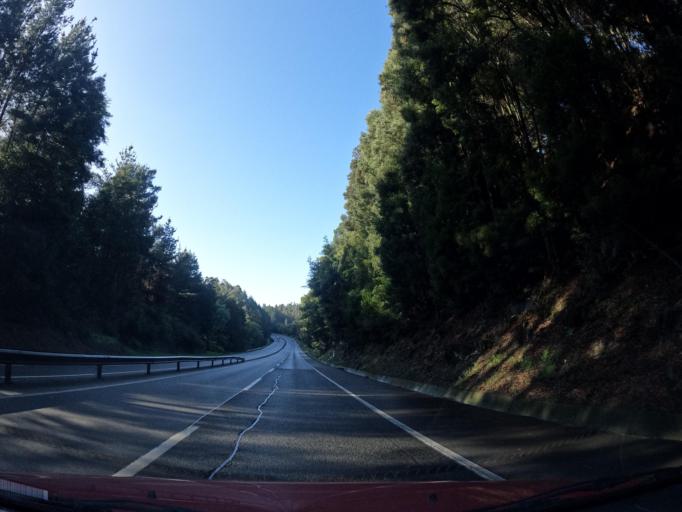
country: CL
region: Biobio
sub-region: Provincia de Concepcion
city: Penco
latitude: -36.7603
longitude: -72.9608
